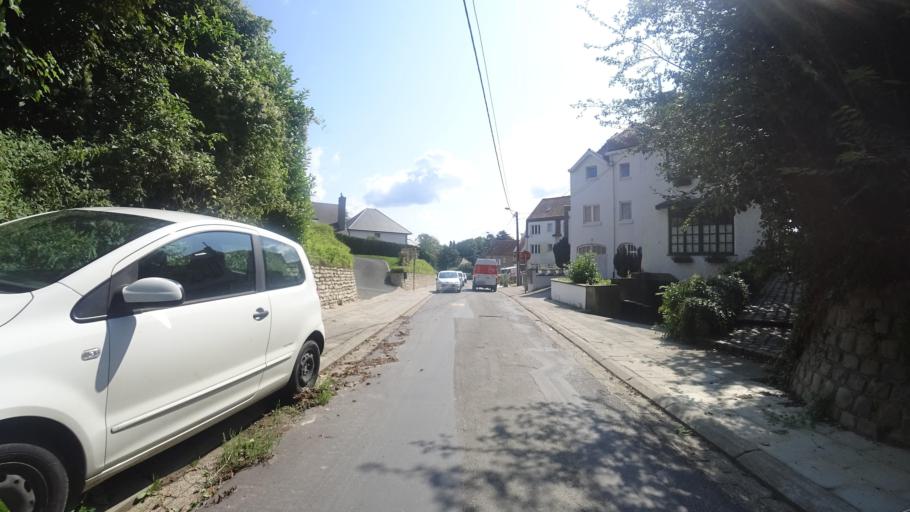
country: BE
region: Flanders
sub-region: Provincie Vlaams-Brabant
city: Tervuren
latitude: 50.8347
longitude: 4.5222
